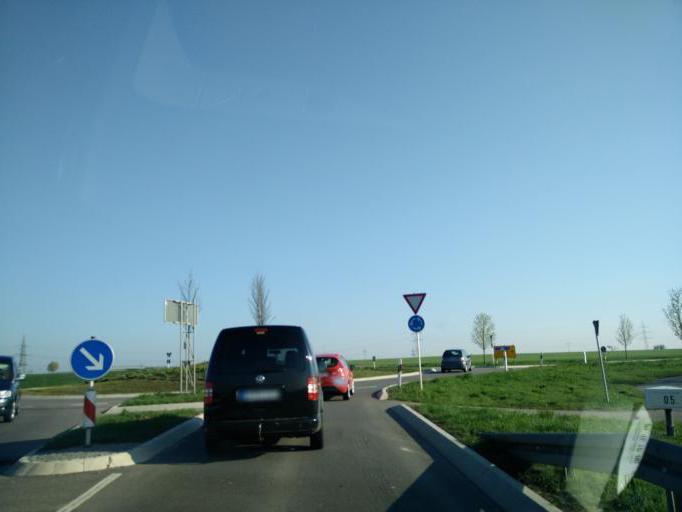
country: DE
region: Baden-Wuerttemberg
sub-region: Regierungsbezirk Stuttgart
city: Herrenberg
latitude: 48.6145
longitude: 8.8525
